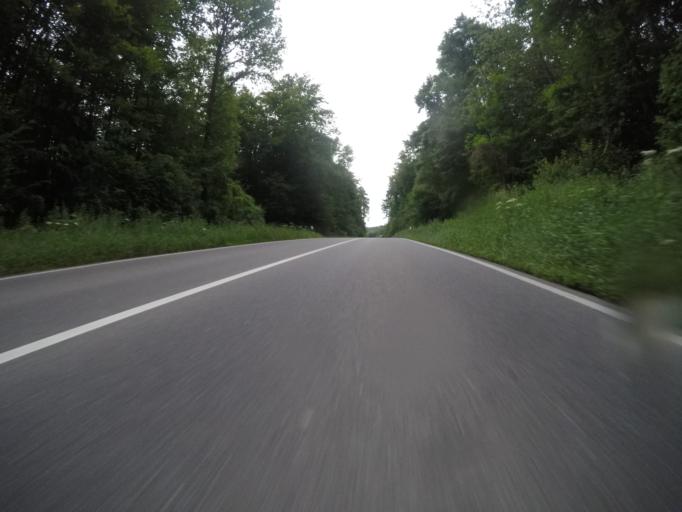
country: DE
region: Baden-Wuerttemberg
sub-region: Regierungsbezirk Stuttgart
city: Rutesheim
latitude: 48.8323
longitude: 8.9690
